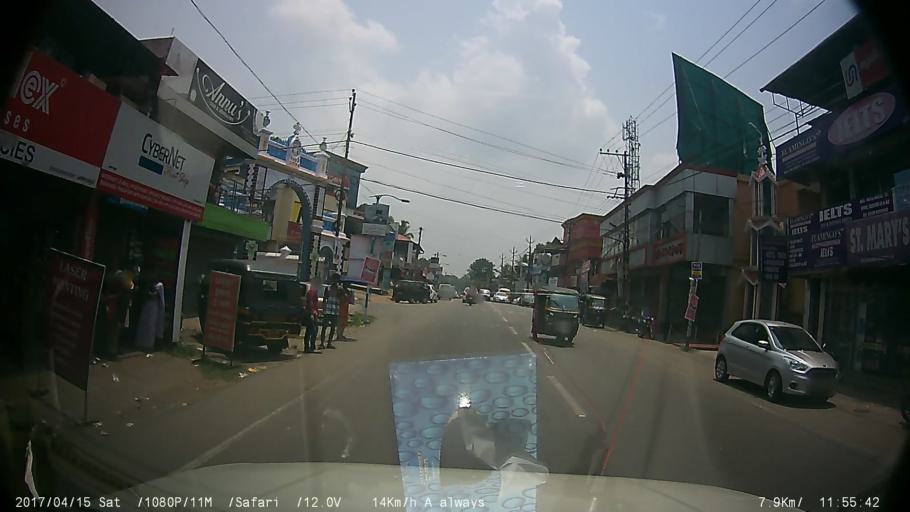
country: IN
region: Kerala
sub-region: Kottayam
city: Changanacheri
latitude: 9.4490
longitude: 76.5437
